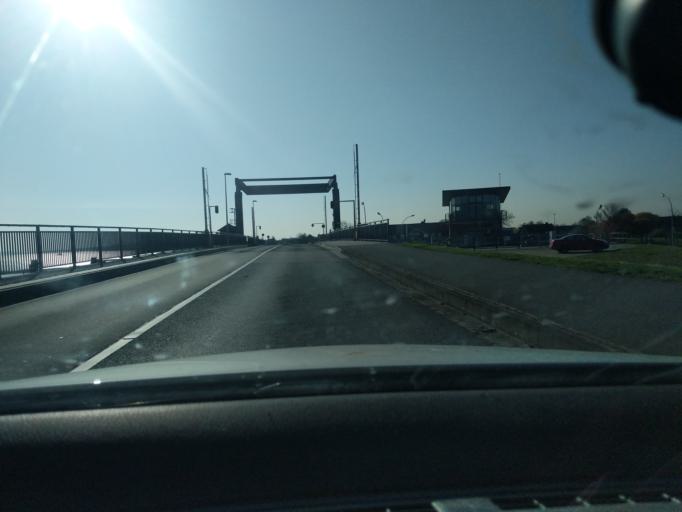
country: DE
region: Lower Saxony
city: Grunendeich
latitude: 53.5718
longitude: 9.6325
